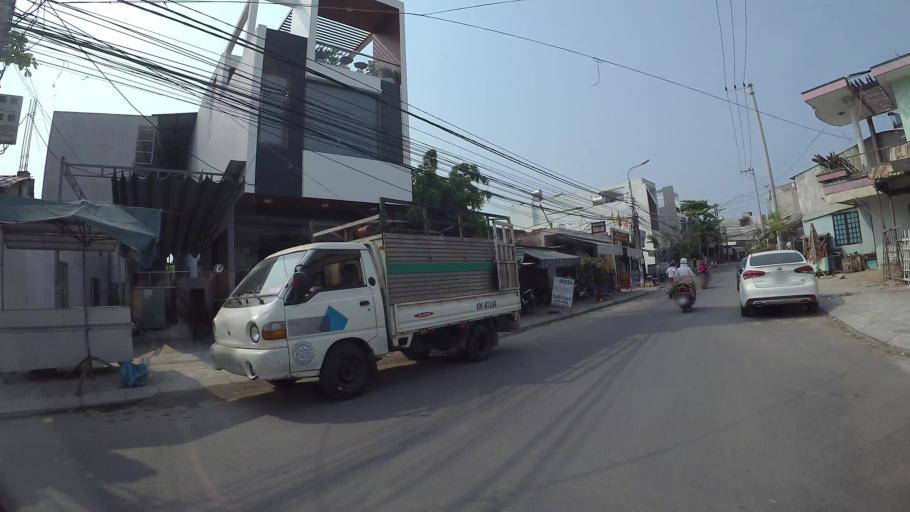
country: VN
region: Da Nang
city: Lien Chieu
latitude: 16.0611
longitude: 108.1573
